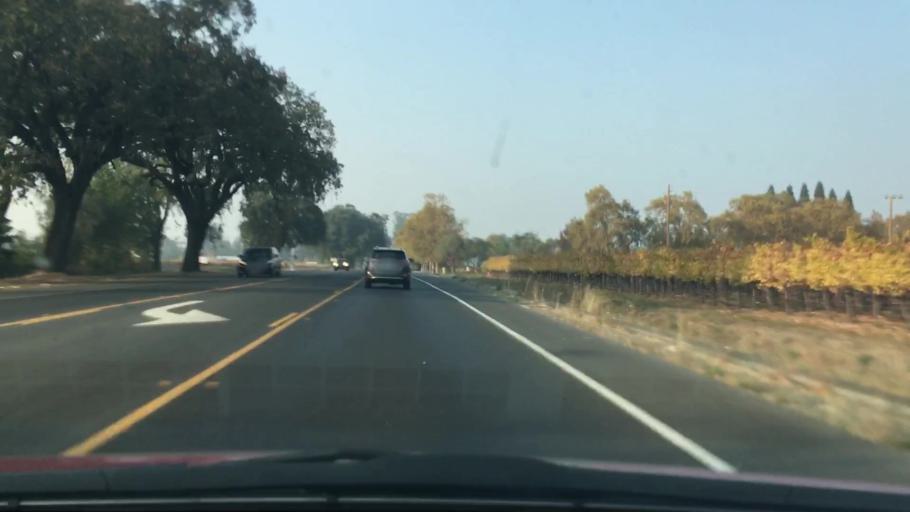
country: US
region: California
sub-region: Napa County
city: Saint Helena
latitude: 38.4719
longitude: -122.4323
